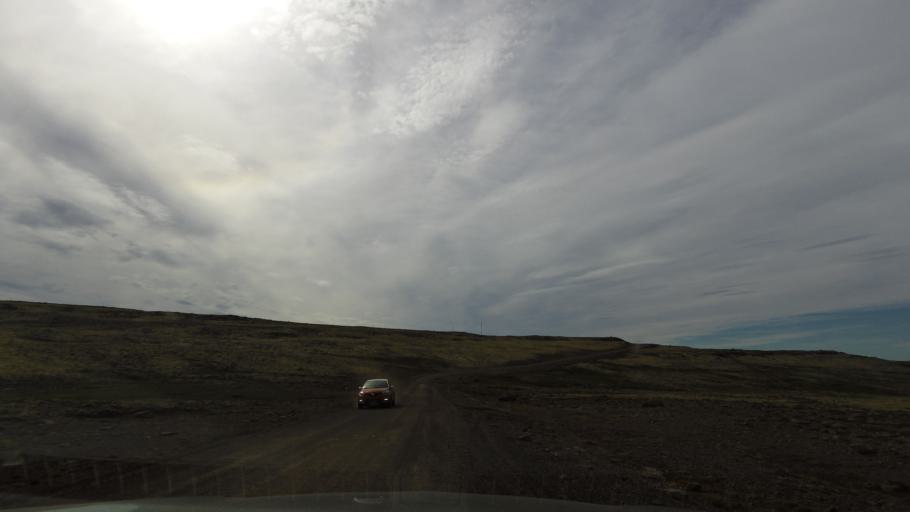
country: IS
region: West
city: Olafsvik
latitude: 65.5422
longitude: -24.3123
